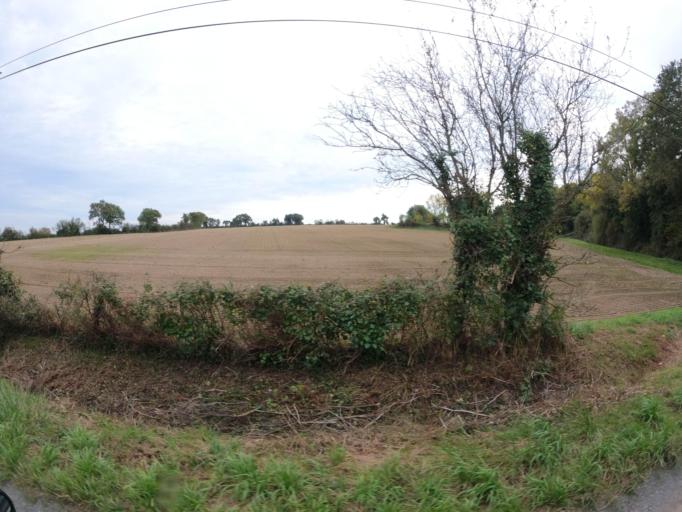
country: FR
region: Pays de la Loire
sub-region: Departement de Maine-et-Loire
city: Saint-Christophe-du-Bois
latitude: 47.0223
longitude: -0.9819
